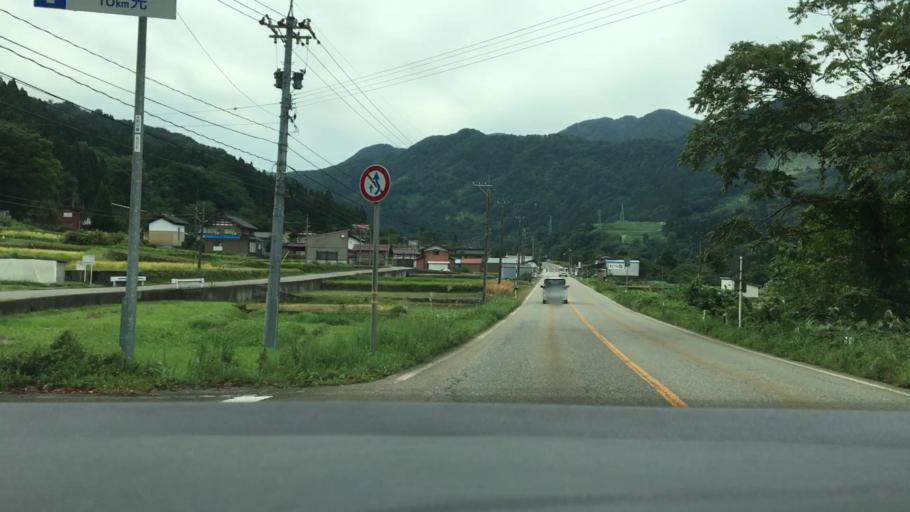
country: JP
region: Ishikawa
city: Tsurugi-asahimachi
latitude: 36.3131
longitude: 136.6474
